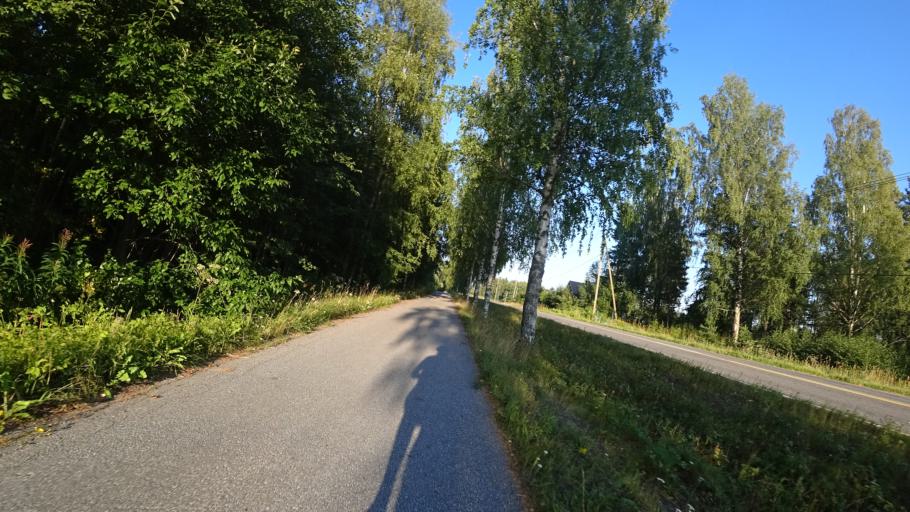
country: FI
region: Pirkanmaa
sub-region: Tampere
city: Nokia
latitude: 61.4681
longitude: 23.3985
